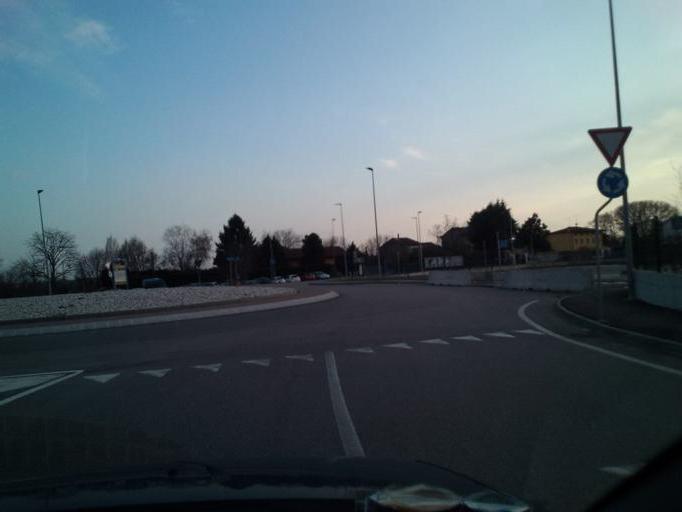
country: IT
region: Veneto
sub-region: Provincia di Verona
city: Dossobuono
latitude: 45.3988
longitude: 10.9021
